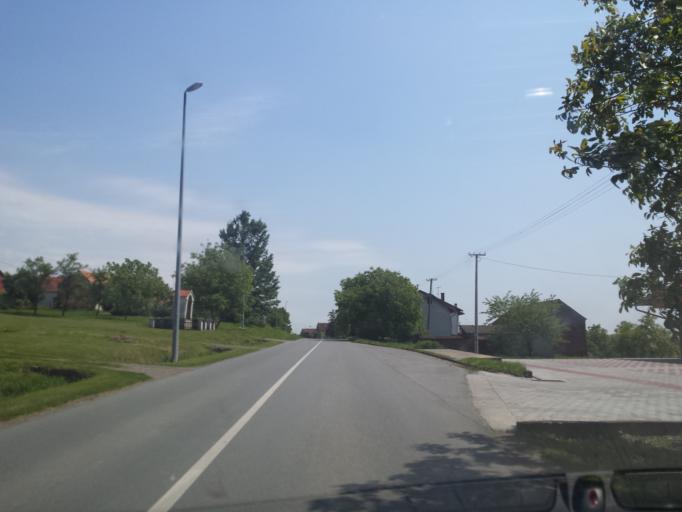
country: HR
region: Brodsko-Posavska
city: Oriovac
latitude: 45.1591
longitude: 17.7745
